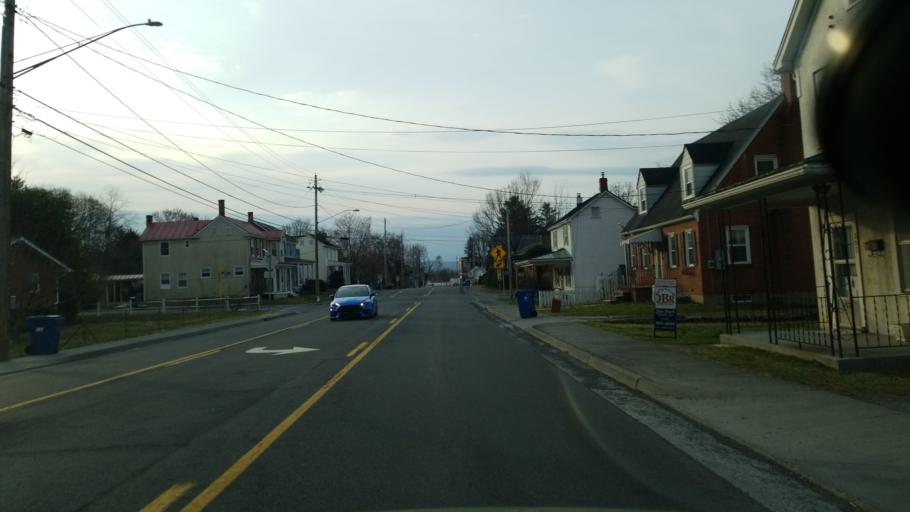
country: US
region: Virginia
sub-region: Clarke County
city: Berryville
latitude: 39.1549
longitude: -77.9867
